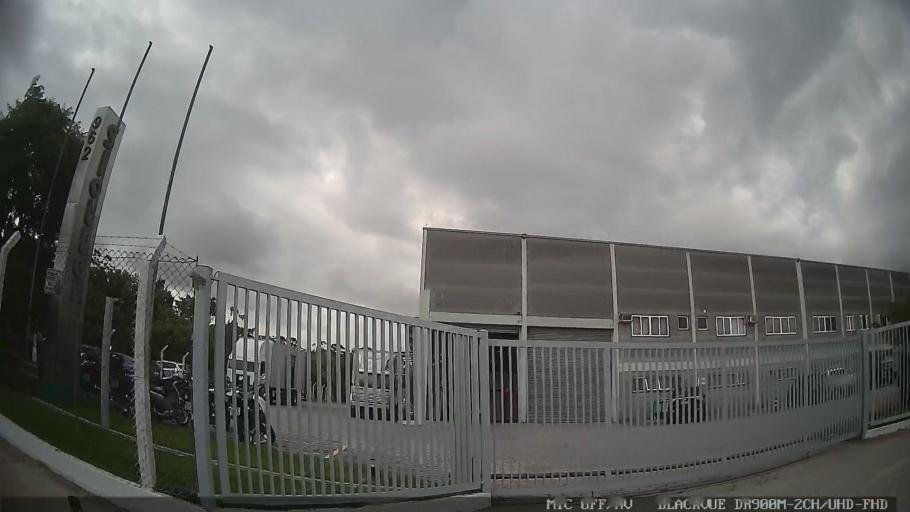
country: BR
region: Sao Paulo
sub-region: Mogi das Cruzes
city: Mogi das Cruzes
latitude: -23.5256
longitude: -46.2134
